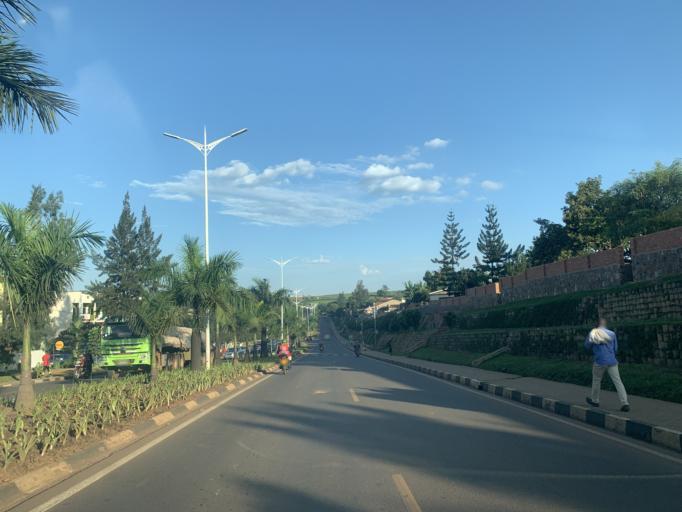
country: RW
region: Kigali
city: Kigali
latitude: -1.9623
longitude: 30.1235
